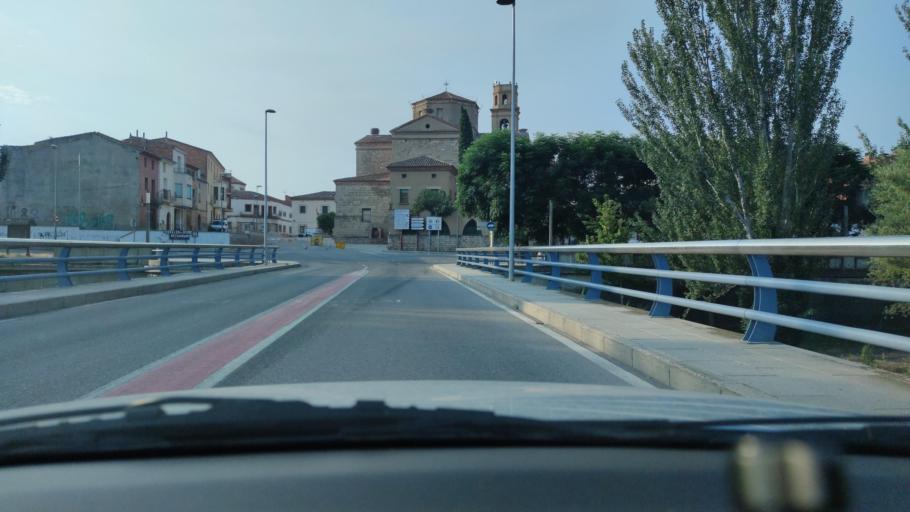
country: ES
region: Catalonia
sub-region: Provincia de Lleida
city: Torres de Segre
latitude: 41.5362
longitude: 0.5126
